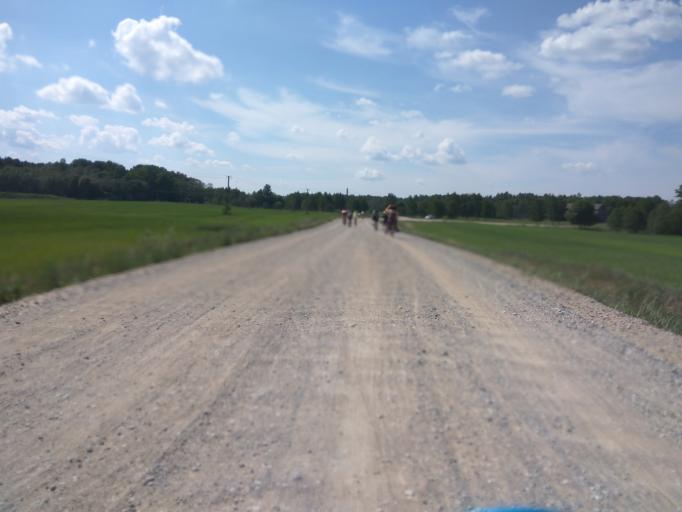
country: LV
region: Kuldigas Rajons
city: Kuldiga
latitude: 56.9411
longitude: 21.9732
